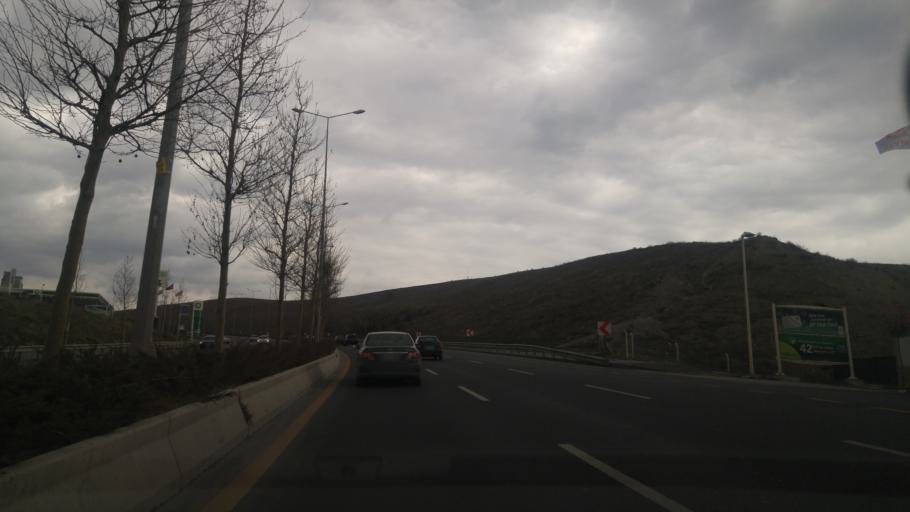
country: TR
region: Ankara
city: Mamak
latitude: 39.8846
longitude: 32.9190
